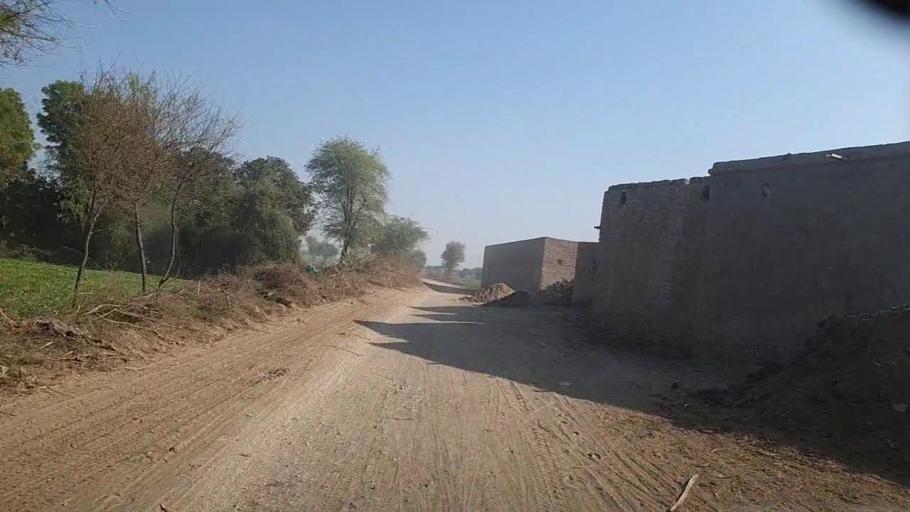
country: PK
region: Sindh
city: Darya Khan Marri
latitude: 26.6726
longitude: 68.3237
